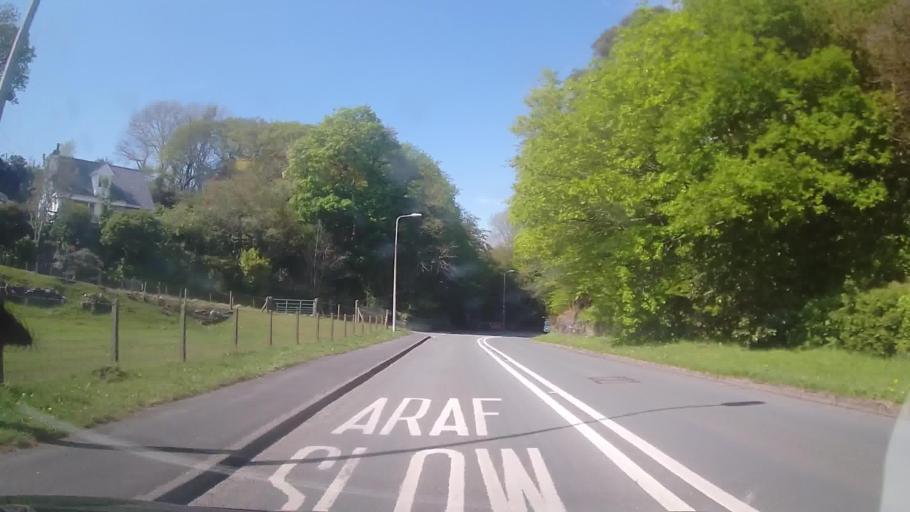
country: GB
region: Wales
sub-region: Gwynedd
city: Porthmadog
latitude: 52.9227
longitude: -4.1340
